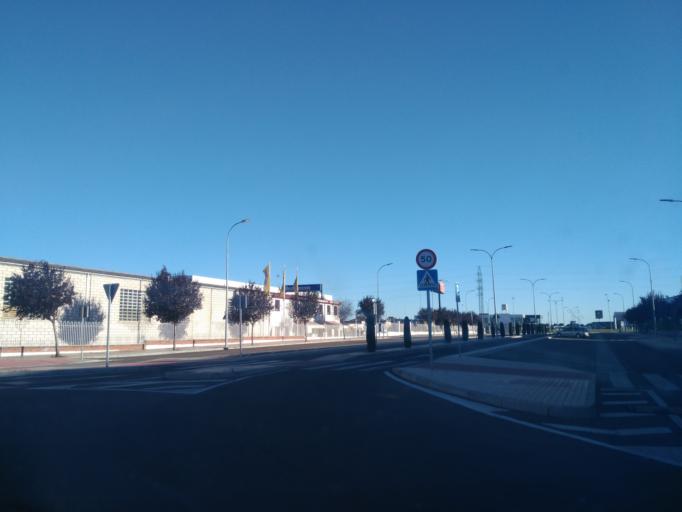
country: ES
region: Castille and Leon
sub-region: Provincia de Salamanca
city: Carbajosa de la Sagrada
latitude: 40.9446
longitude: -5.6559
